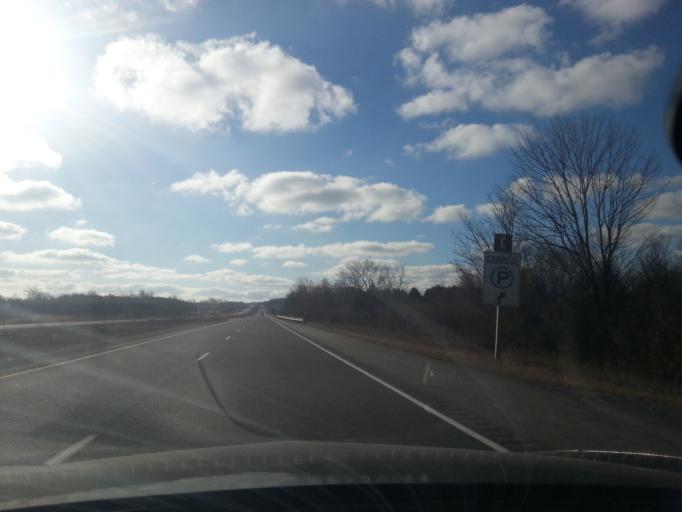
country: CA
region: Ontario
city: Omemee
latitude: 44.1940
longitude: -78.4559
